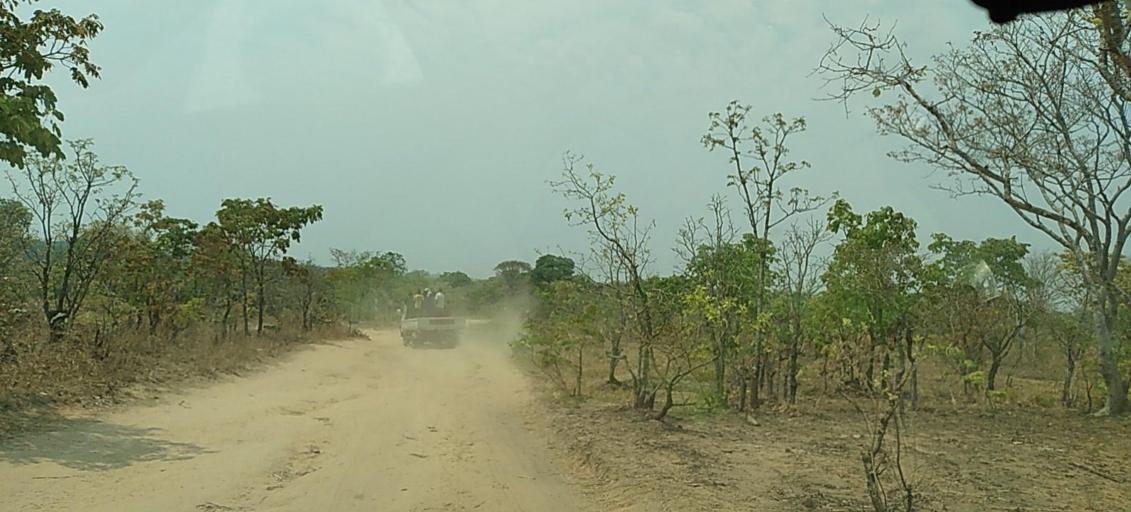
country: ZM
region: North-Western
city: Kabompo
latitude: -13.4805
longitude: 24.4589
